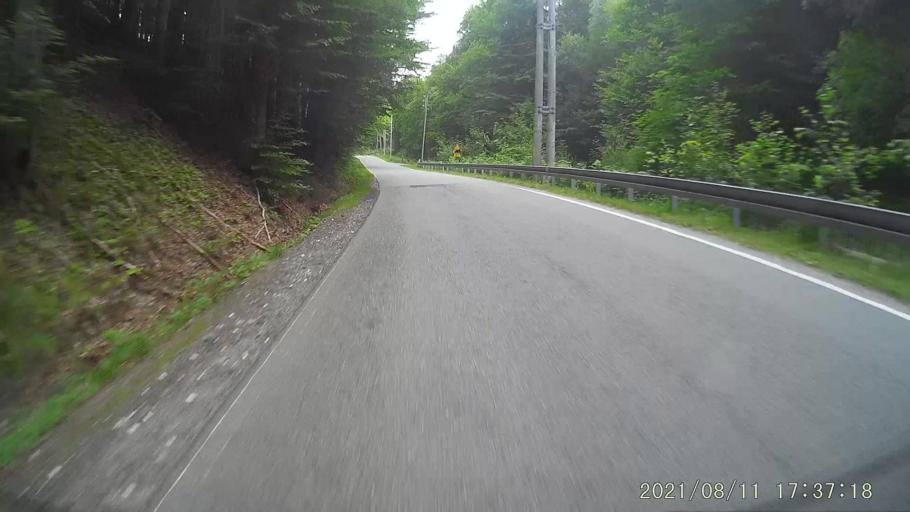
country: PL
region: Lower Silesian Voivodeship
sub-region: Powiat klodzki
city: Duszniki-Zdroj
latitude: 50.3374
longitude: 16.4051
